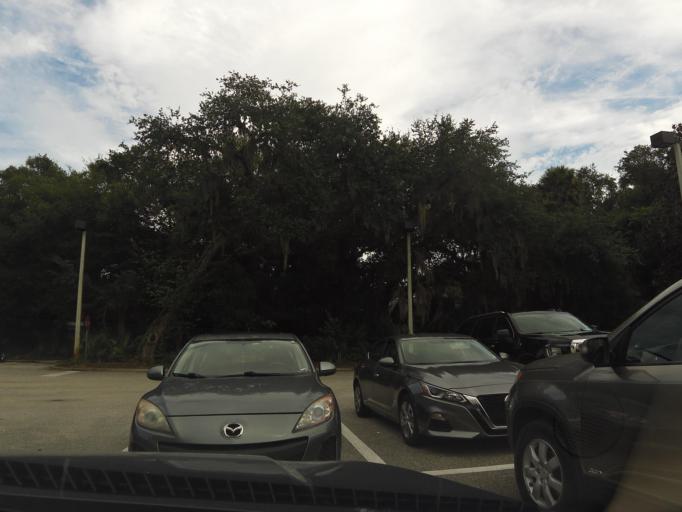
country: US
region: Florida
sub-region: Flagler County
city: Palm Coast
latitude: 29.6011
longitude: -81.1963
